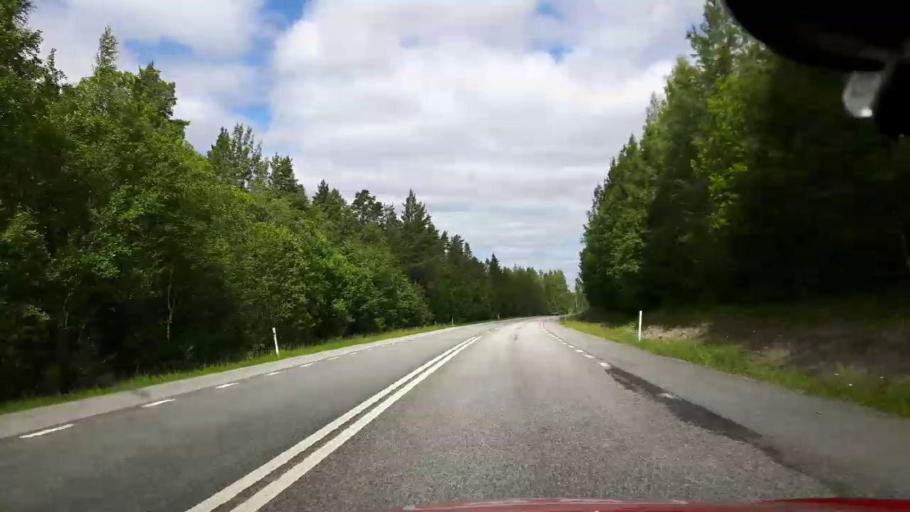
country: SE
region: Jaemtland
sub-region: Braecke Kommun
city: Braecke
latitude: 62.7308
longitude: 15.4360
